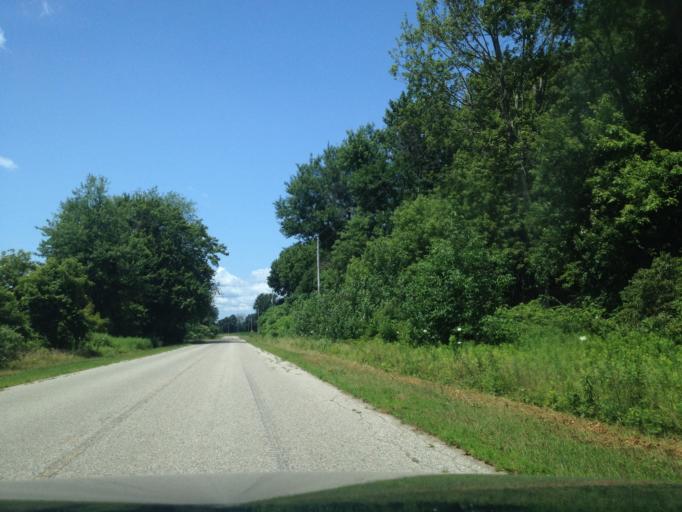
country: CA
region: Ontario
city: Aylmer
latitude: 42.6414
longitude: -80.7764
